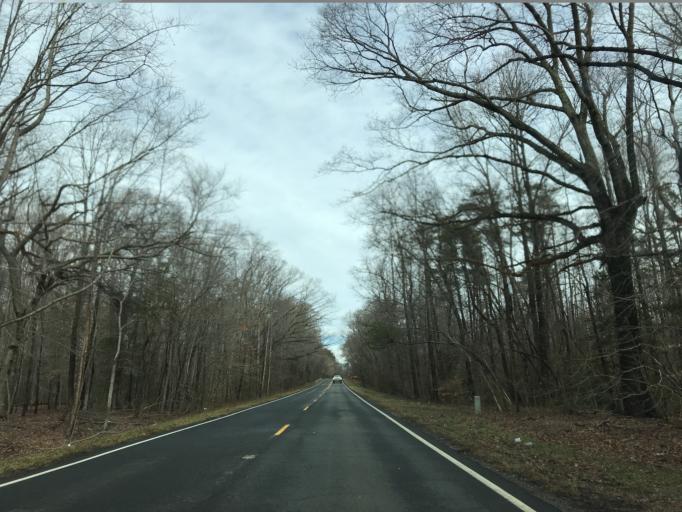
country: US
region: Virginia
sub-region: King George County
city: Dahlgren
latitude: 38.2687
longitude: -77.0461
